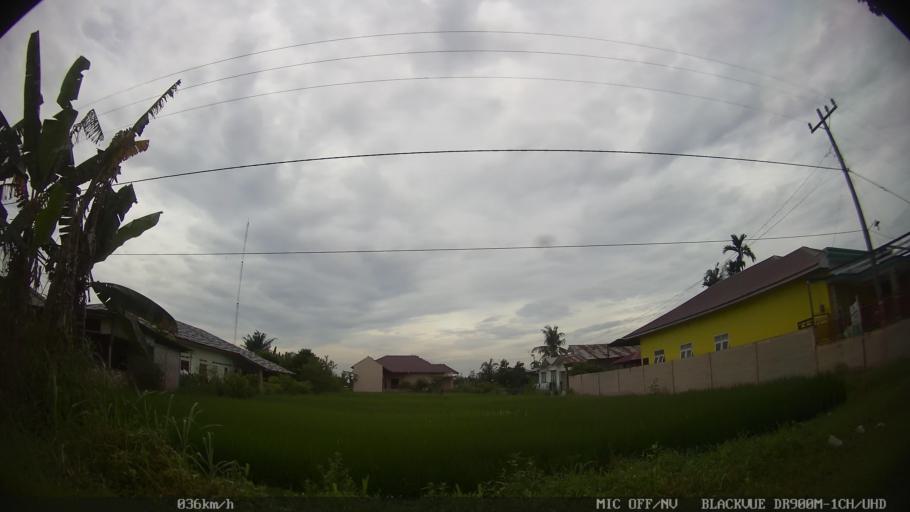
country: ID
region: North Sumatra
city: Sunggal
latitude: 3.5836
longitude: 98.5652
